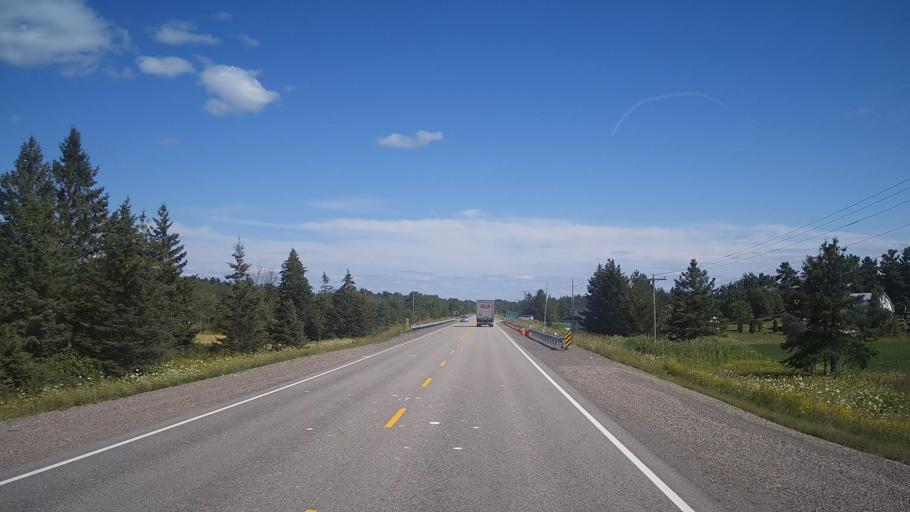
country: CA
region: Ontario
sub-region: Nipissing District
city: North Bay
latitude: 46.3905
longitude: -80.0011
